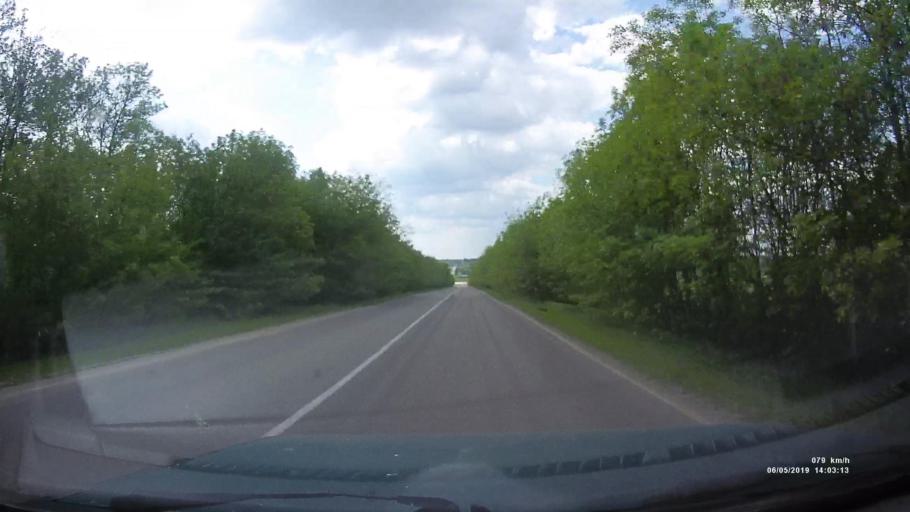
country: RU
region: Rostov
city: Shakhty
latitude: 47.6811
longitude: 40.3502
